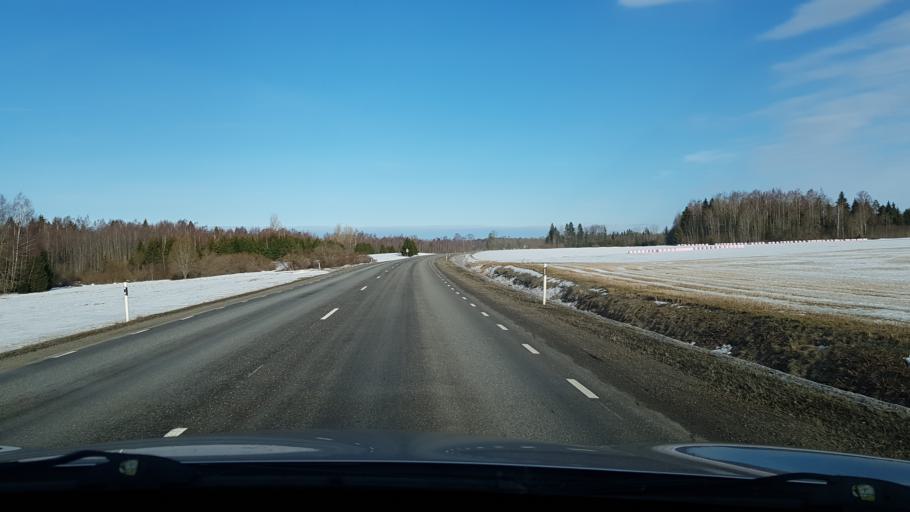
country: EE
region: Viljandimaa
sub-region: Viljandi linn
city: Viljandi
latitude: 58.4303
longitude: 25.5956
